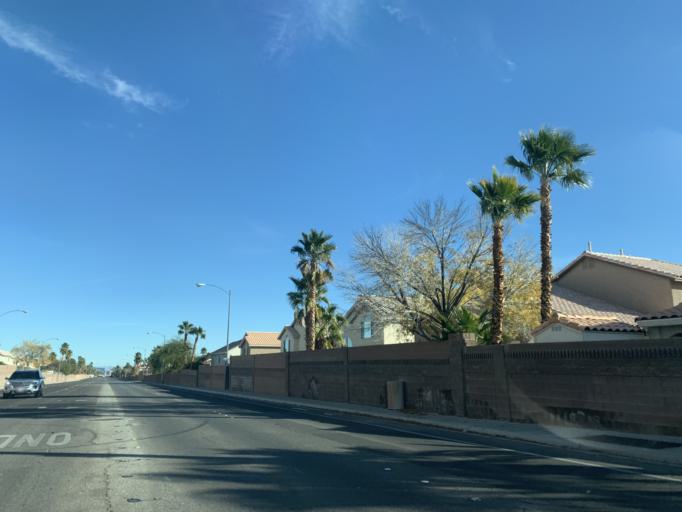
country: US
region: Nevada
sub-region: Clark County
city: Summerlin South
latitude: 36.1262
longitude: -115.3060
